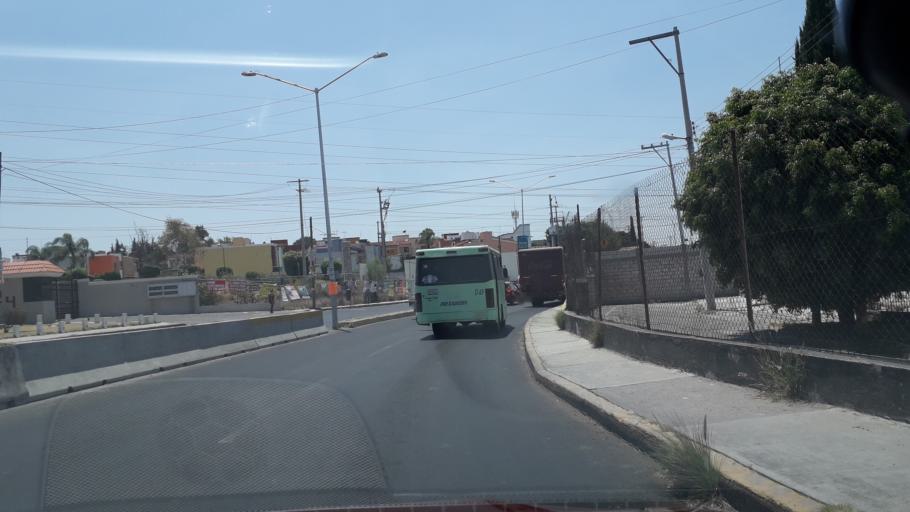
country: MX
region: Puebla
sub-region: Puebla
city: Galaxia la Calera
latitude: 19.0008
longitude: -98.1805
